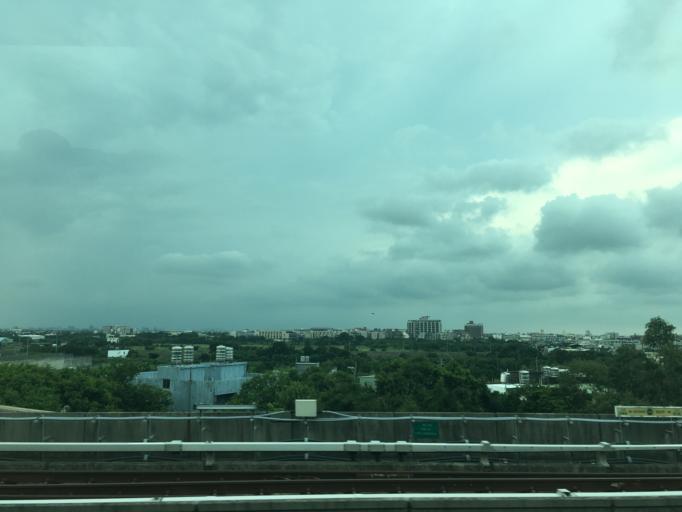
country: TW
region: Taiwan
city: Taoyuan City
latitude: 25.0860
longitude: 121.2672
